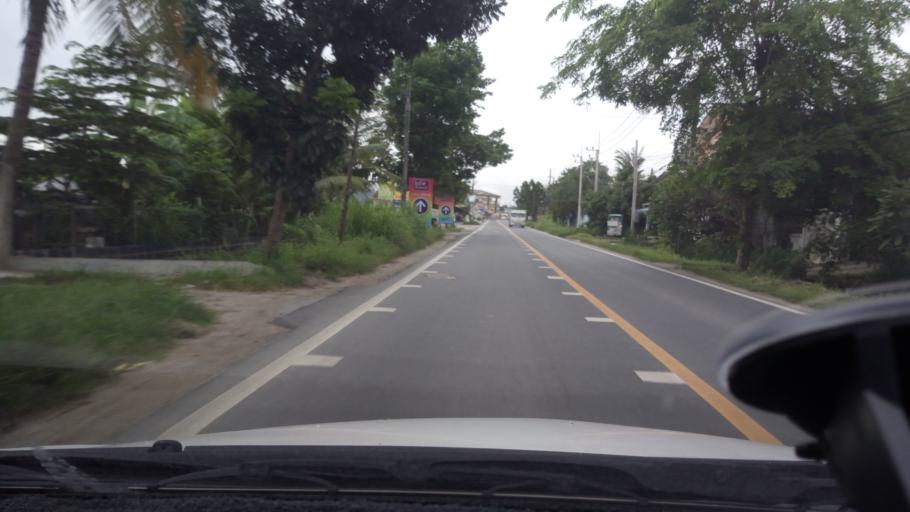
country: TH
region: Chon Buri
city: Chon Buri
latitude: 13.4002
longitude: 101.0490
